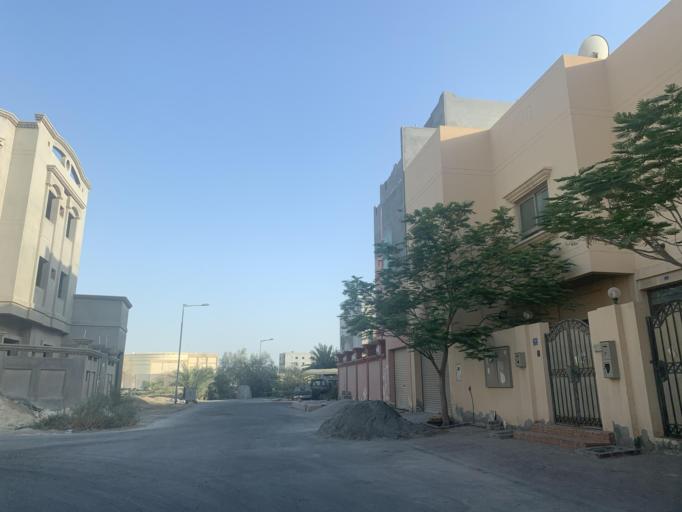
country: BH
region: Manama
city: Jidd Hafs
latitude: 26.2117
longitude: 50.5251
